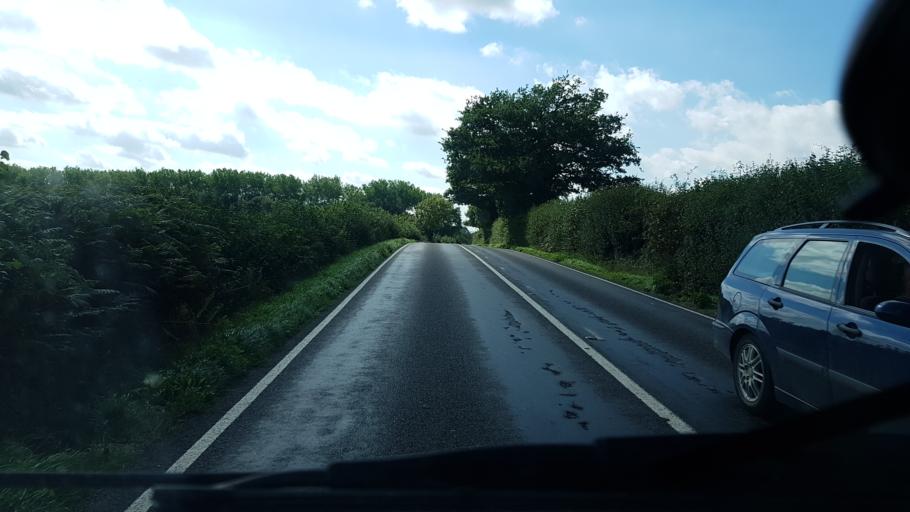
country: GB
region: England
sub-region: West Sussex
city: Rudgwick
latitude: 51.0878
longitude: -0.3984
